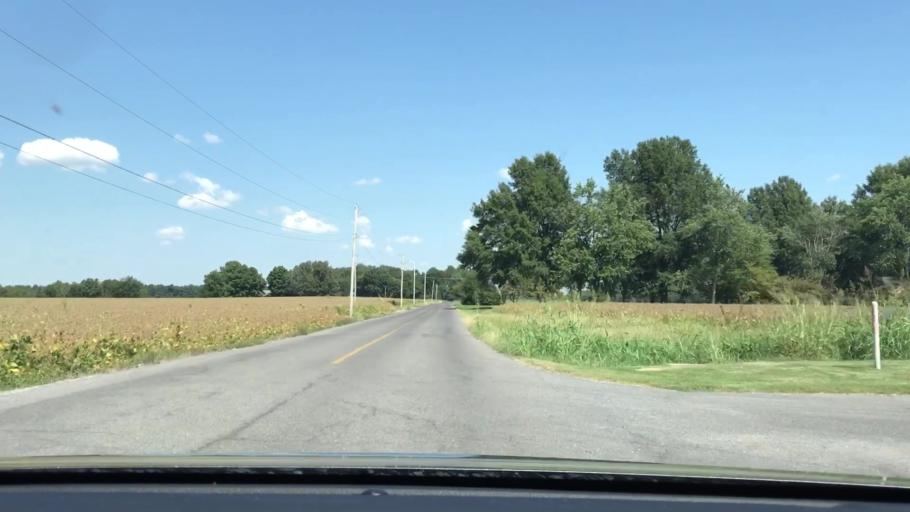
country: US
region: Kentucky
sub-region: Fulton County
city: Fulton
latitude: 36.5179
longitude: -88.9014
